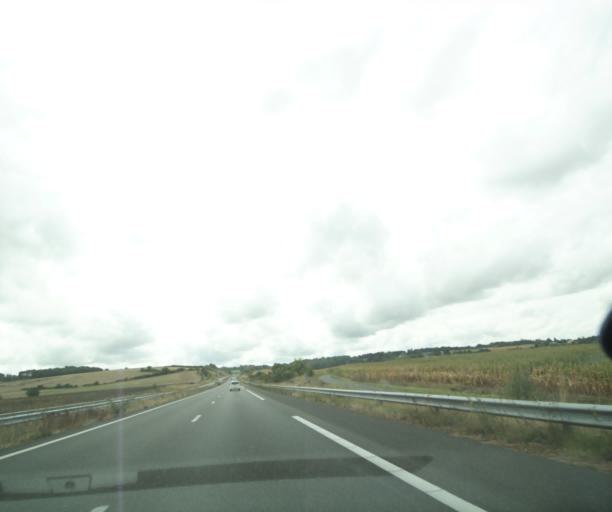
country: FR
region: Poitou-Charentes
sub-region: Departement de la Charente-Maritime
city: Mirambeau
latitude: 45.4196
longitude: -0.6037
